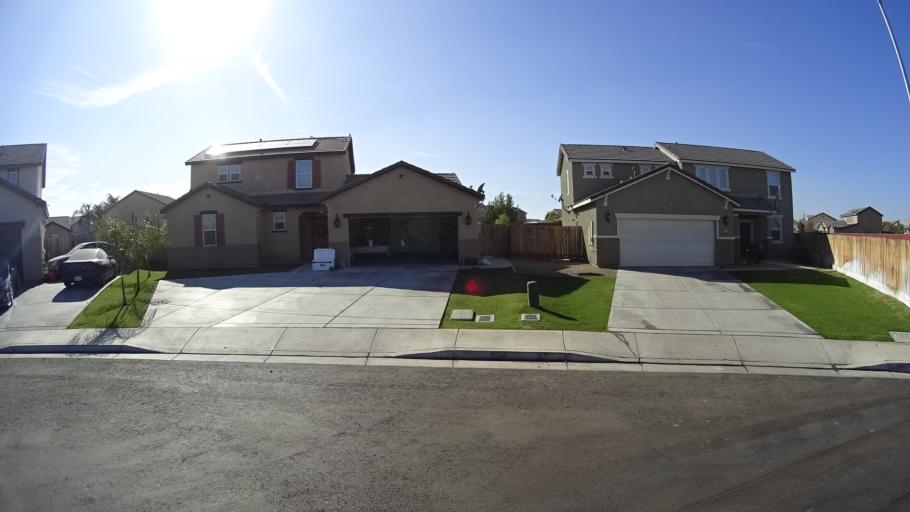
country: US
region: California
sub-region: Kern County
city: Greenfield
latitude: 35.2908
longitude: -119.0617
